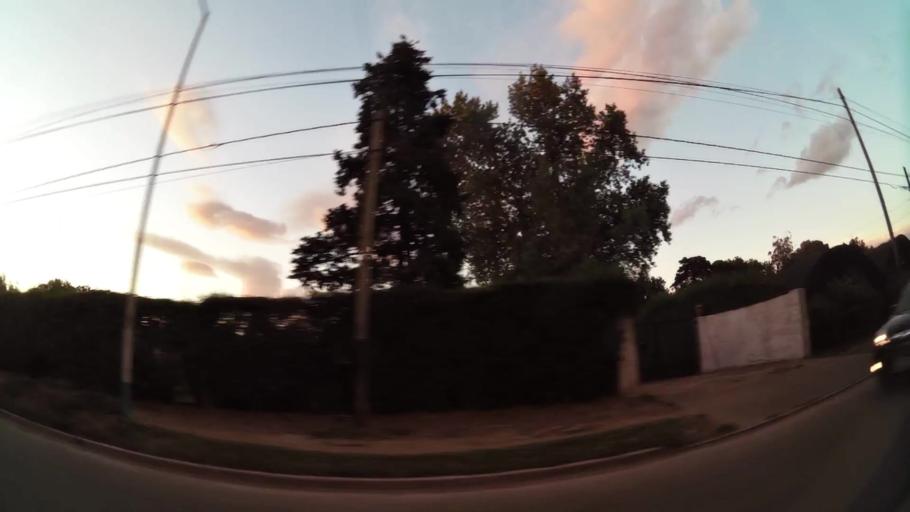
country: AR
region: Buenos Aires
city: Santa Catalina - Dique Lujan
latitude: -34.4755
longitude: -58.7680
